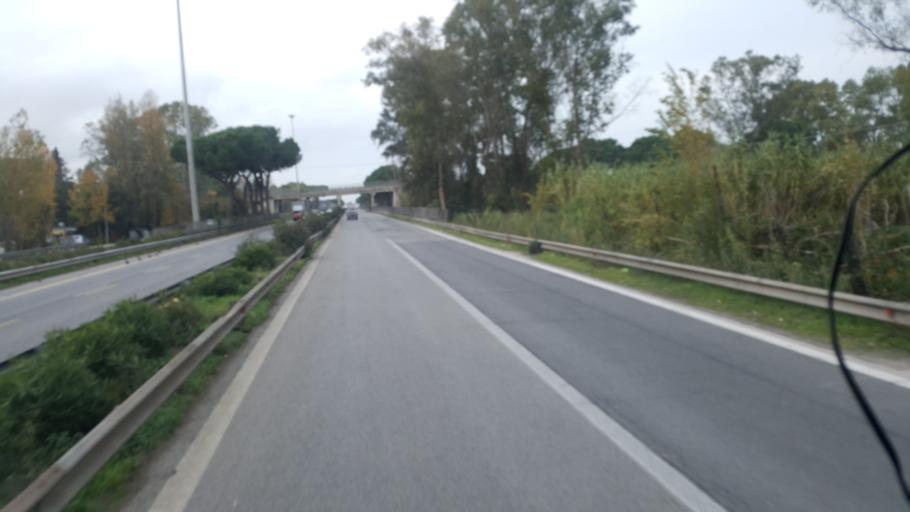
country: IT
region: Latium
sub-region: Provincia di Latina
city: Borgo Podgora
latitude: 41.4877
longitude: 12.8482
